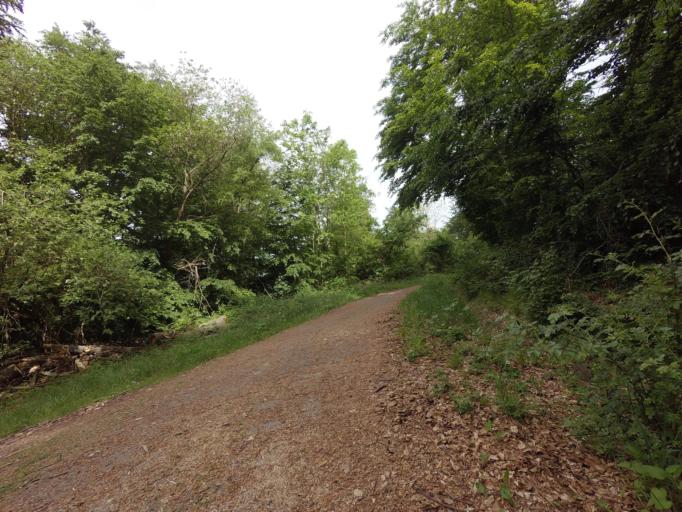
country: DE
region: Lower Saxony
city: Erkerode
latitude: 52.2020
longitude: 10.7188
